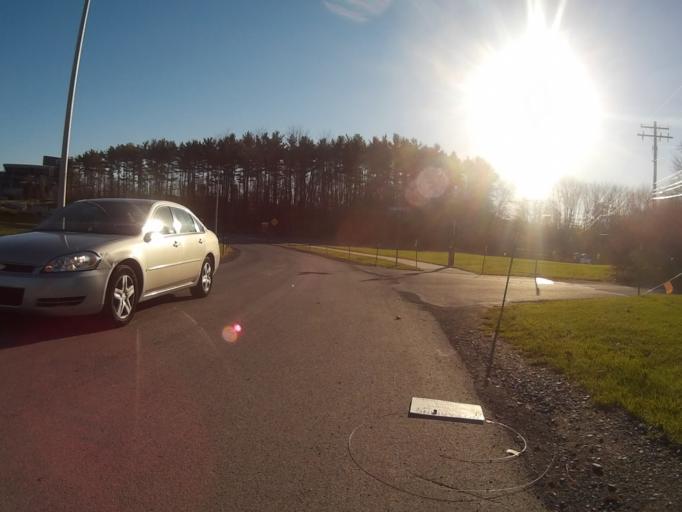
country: US
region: Pennsylvania
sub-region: Centre County
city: State College
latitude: 40.8189
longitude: -77.8589
